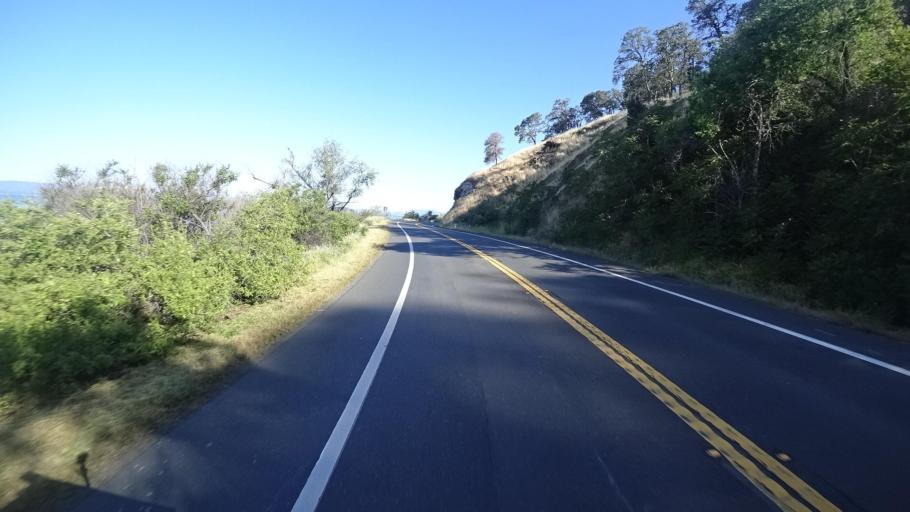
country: US
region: California
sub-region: Lake County
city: Lucerne
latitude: 39.0618
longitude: -122.7828
